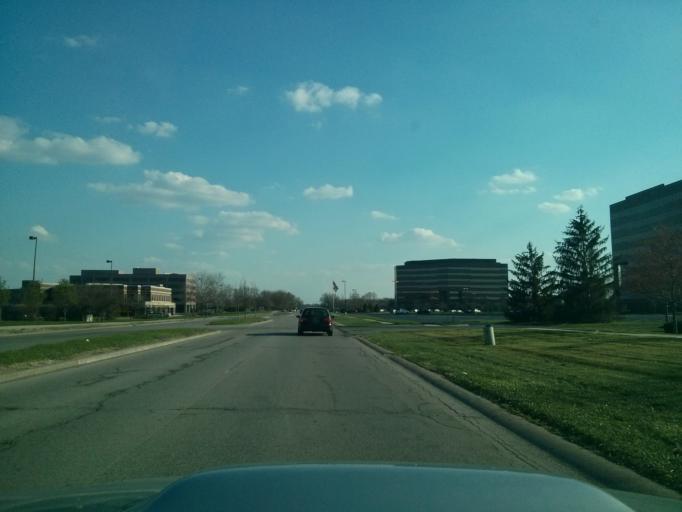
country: US
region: Indiana
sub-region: Hamilton County
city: Carmel
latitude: 39.9610
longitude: -86.1553
